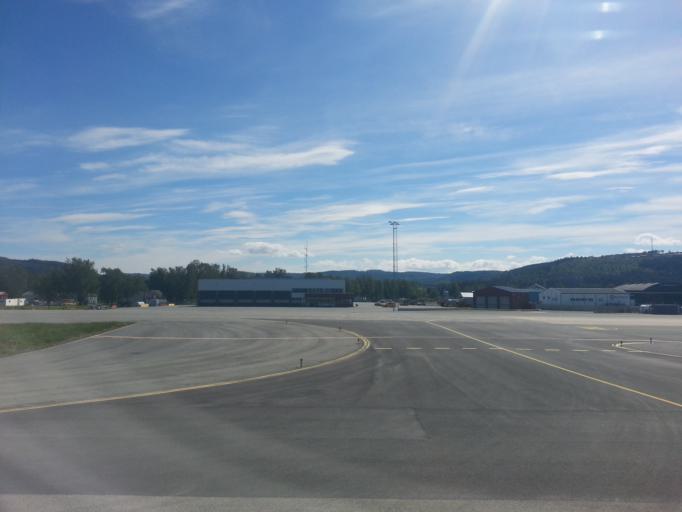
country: NO
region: Nord-Trondelag
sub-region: Stjordal
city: Stjordalshalsen
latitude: 63.4560
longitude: 10.9278
